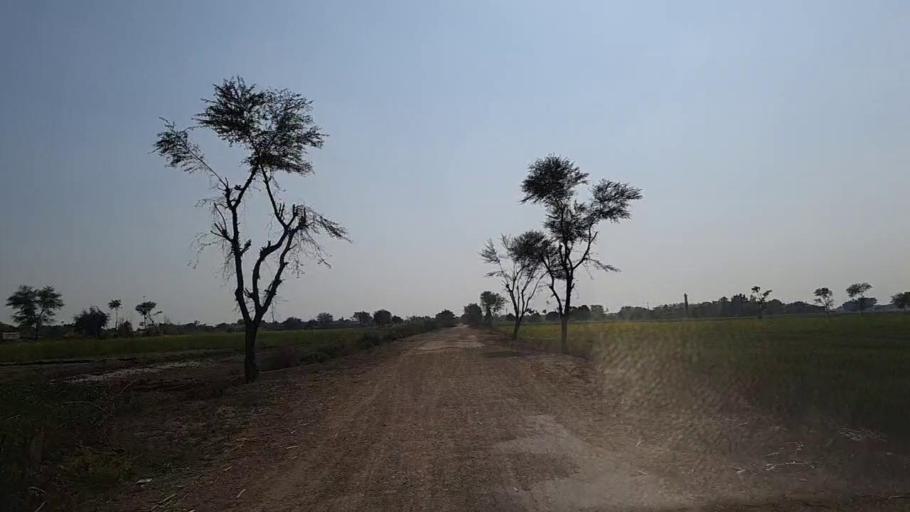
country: PK
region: Sindh
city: Jam Sahib
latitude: 26.2686
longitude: 68.5288
